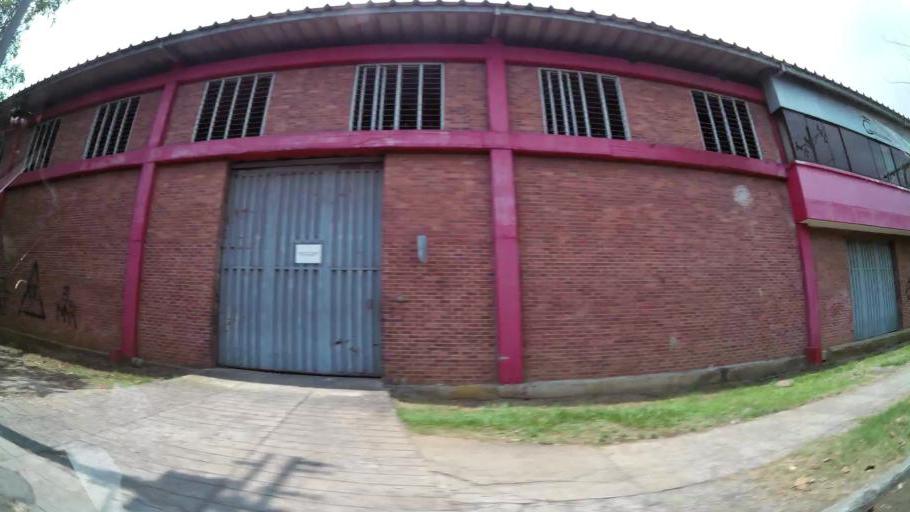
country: CO
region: Valle del Cauca
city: Cali
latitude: 3.4775
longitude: -76.5023
